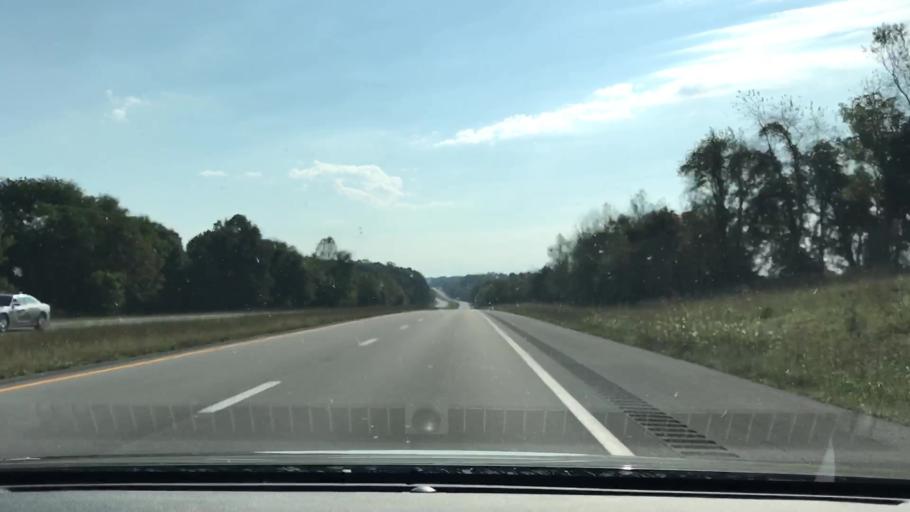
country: US
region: Kentucky
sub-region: Adair County
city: Columbia
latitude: 37.0683
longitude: -85.2071
